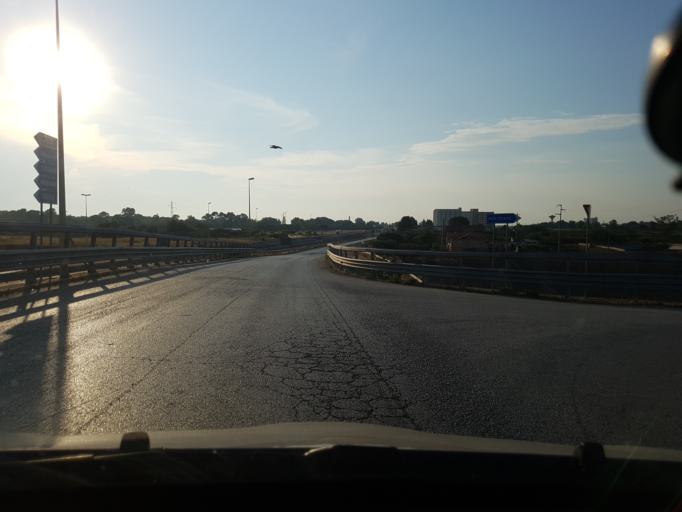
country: IT
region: Apulia
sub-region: Provincia di Foggia
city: Carapelle
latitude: 41.3951
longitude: 15.6602
